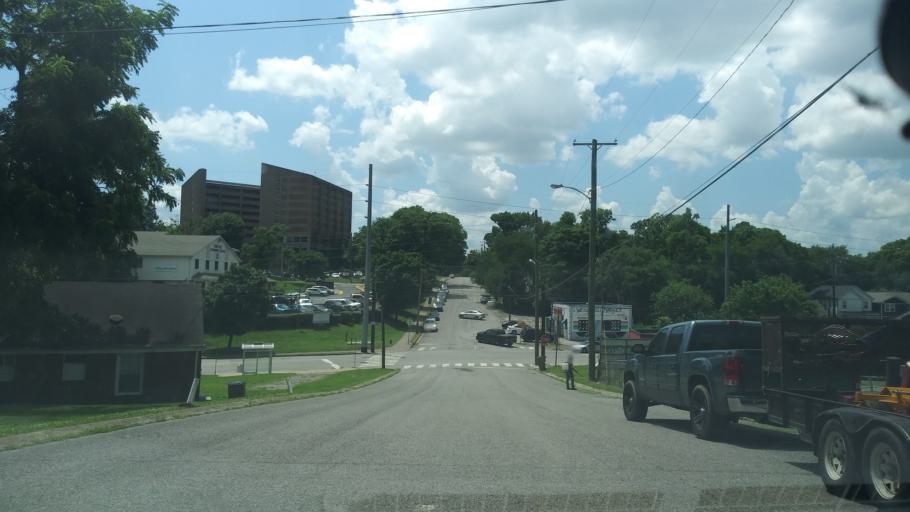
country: US
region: Tennessee
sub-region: Davidson County
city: Nashville
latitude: 36.1317
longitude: -86.7676
